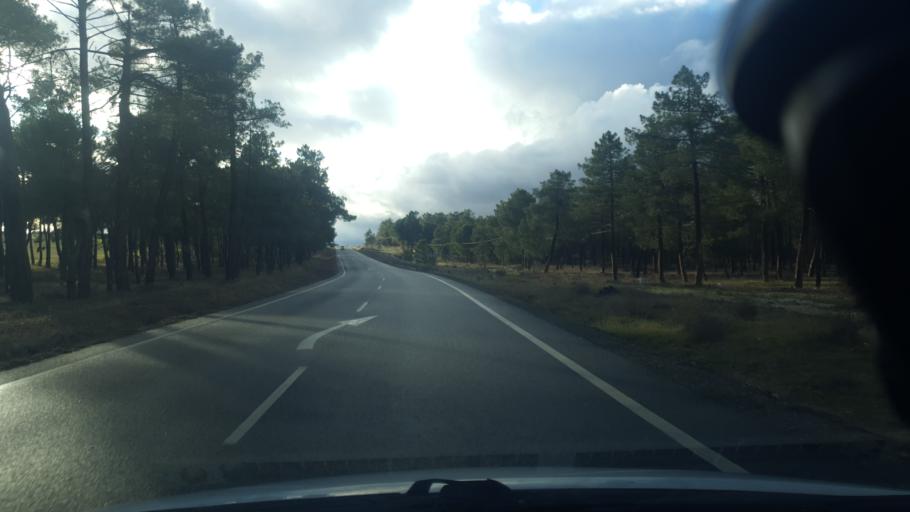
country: ES
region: Castille and Leon
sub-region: Provincia de Segovia
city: Nava de la Asuncion
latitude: 41.1554
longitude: -4.5242
